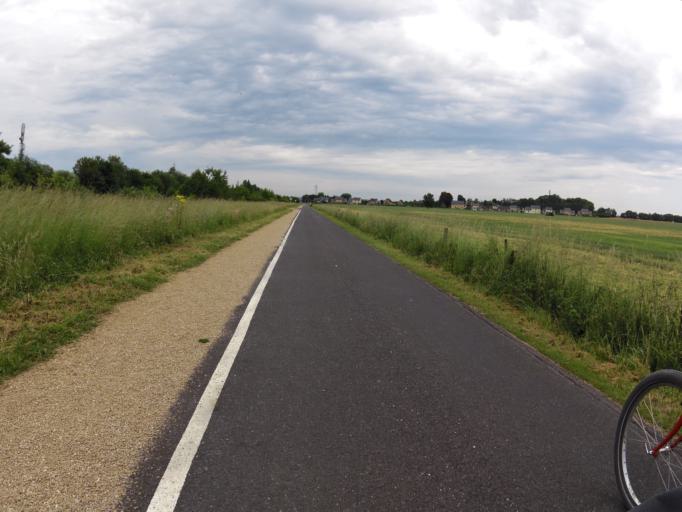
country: FR
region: Champagne-Ardenne
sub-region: Departement des Ardennes
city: Floing
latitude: 49.7116
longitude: 4.9096
